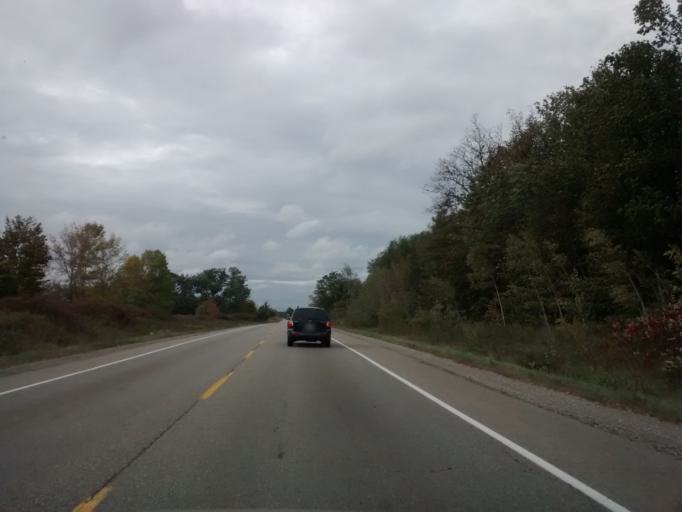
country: CA
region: Ontario
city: Ancaster
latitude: 43.0701
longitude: -79.9764
